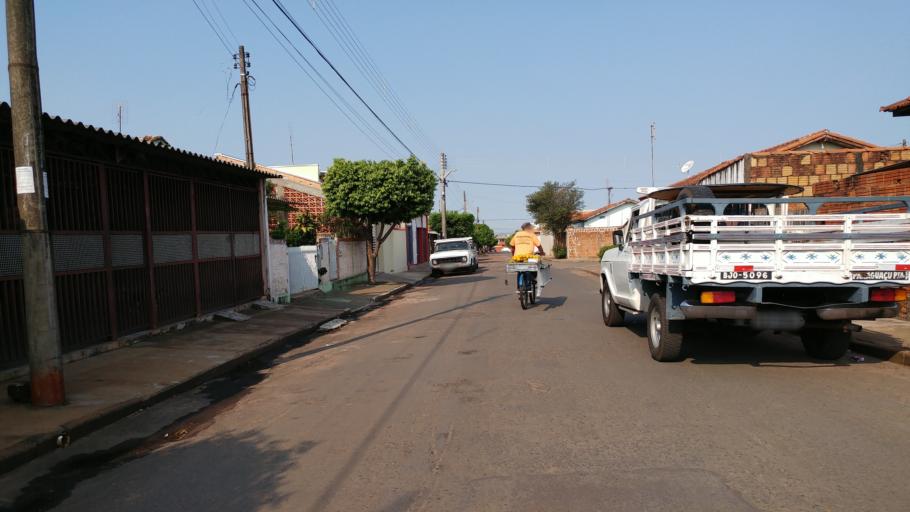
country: BR
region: Sao Paulo
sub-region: Paraguacu Paulista
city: Paraguacu Paulista
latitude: -22.4311
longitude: -50.5817
